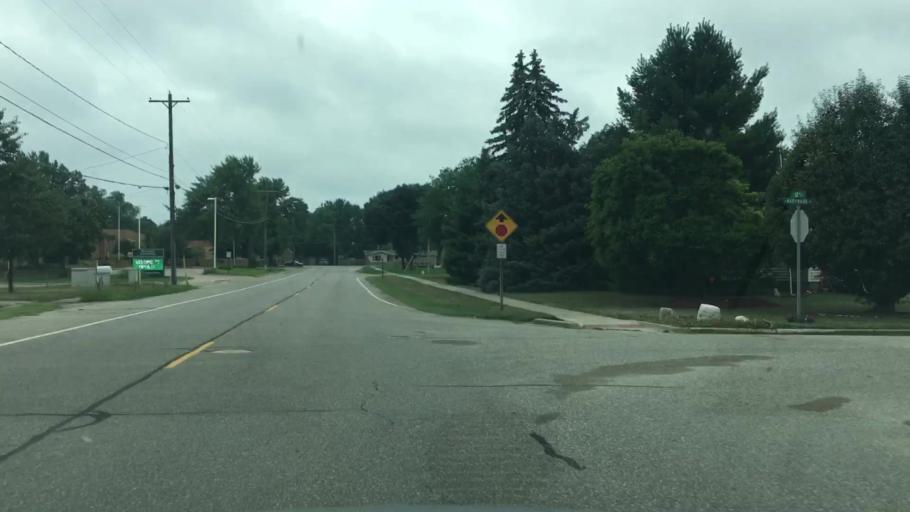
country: US
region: Michigan
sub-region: Ottawa County
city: Jenison
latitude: 42.8906
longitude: -85.8119
